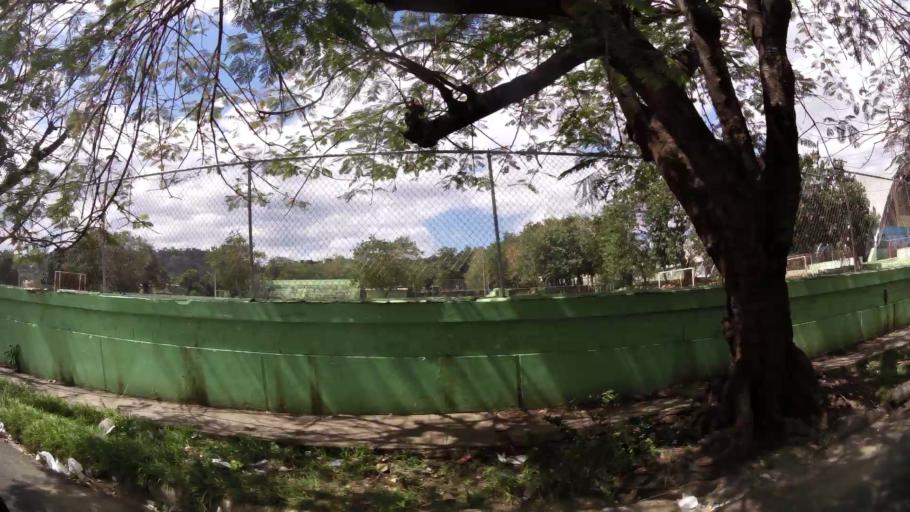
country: DO
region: San Cristobal
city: San Cristobal
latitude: 18.4106
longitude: -70.1140
